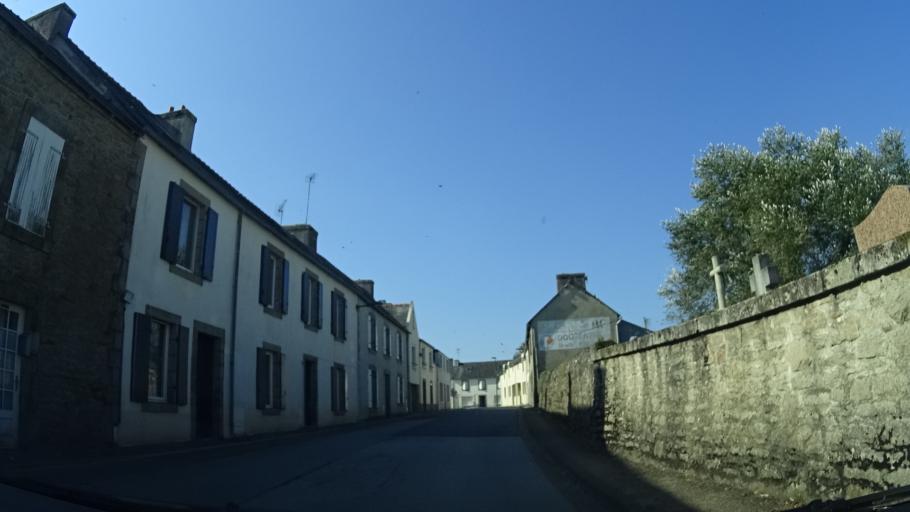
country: FR
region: Brittany
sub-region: Departement du Finistere
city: Plonevez-Porzay
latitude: 48.1261
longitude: -4.2176
